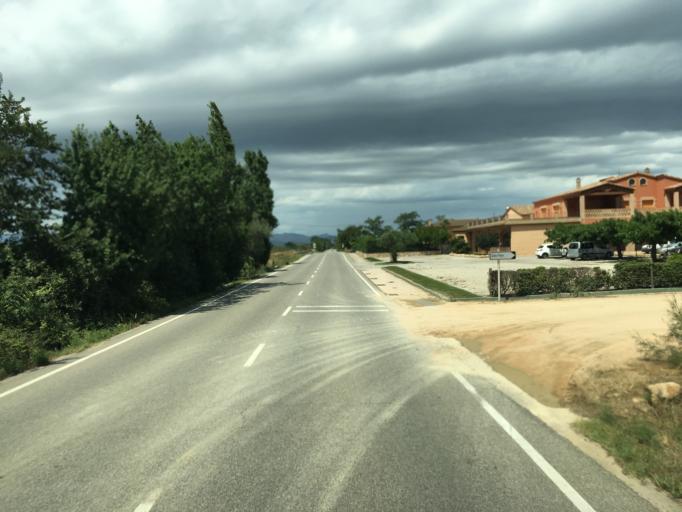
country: ES
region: Catalonia
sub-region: Provincia de Girona
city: Sant Pere Pescador
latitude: 42.2069
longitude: 3.0848
